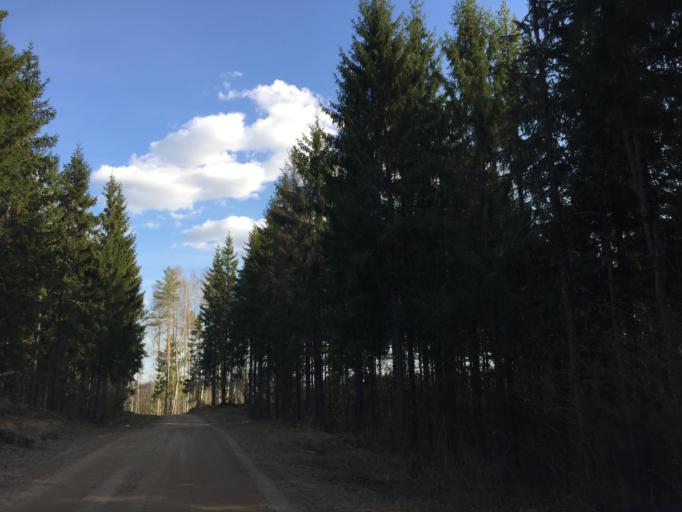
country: EE
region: Tartu
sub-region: Noo vald
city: Noo
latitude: 58.1343
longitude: 26.6287
